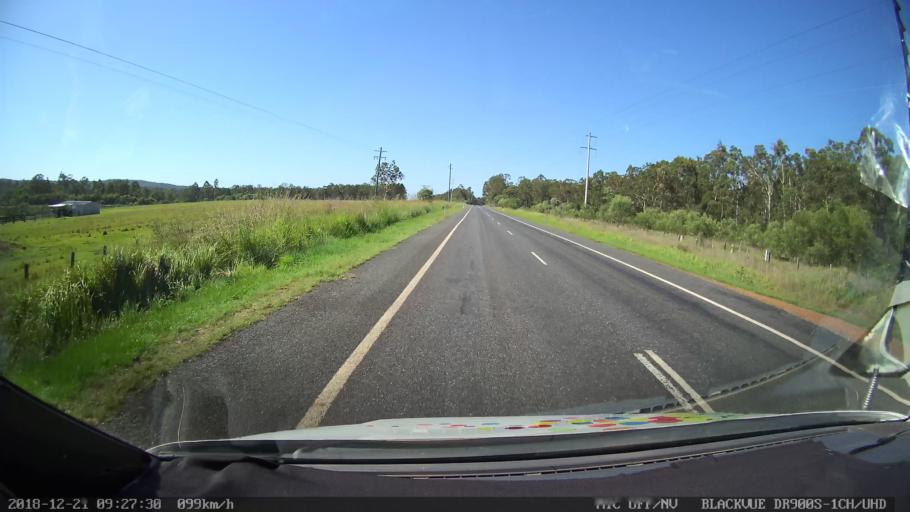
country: AU
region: New South Wales
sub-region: Clarence Valley
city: Maclean
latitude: -29.4036
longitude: 152.9898
